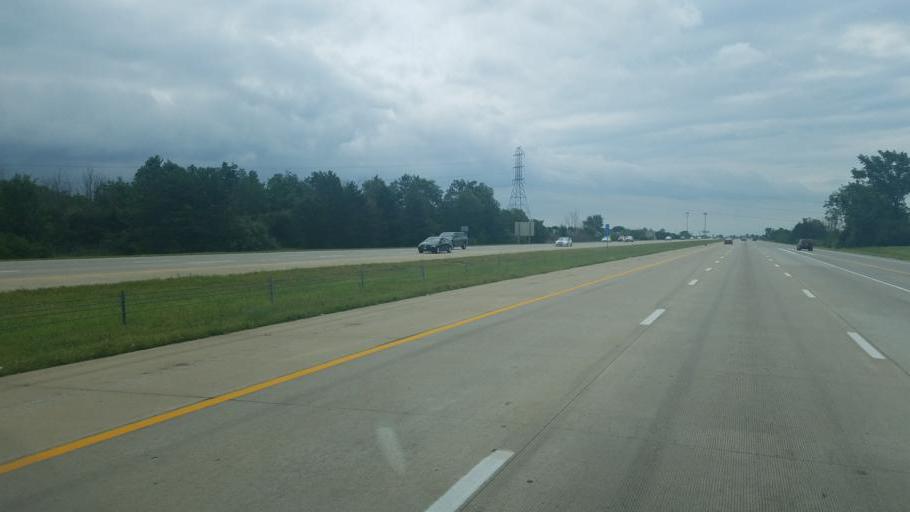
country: US
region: Ohio
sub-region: Franklin County
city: Lincoln Village
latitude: 39.9201
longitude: -83.1154
